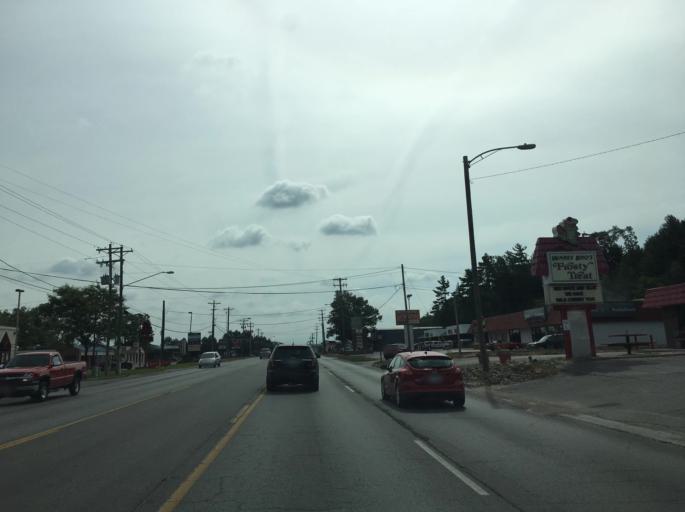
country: US
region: Michigan
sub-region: Grand Traverse County
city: Traverse City
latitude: 44.7334
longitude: -85.6038
